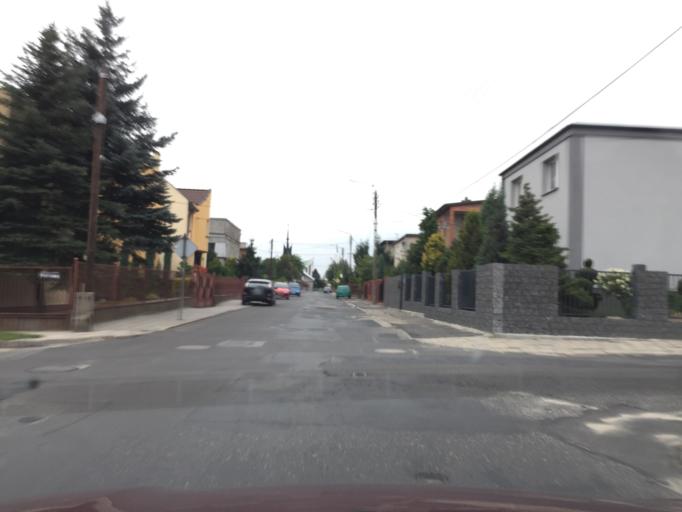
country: PL
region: Greater Poland Voivodeship
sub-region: Kalisz
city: Kalisz
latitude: 51.7765
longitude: 18.0877
